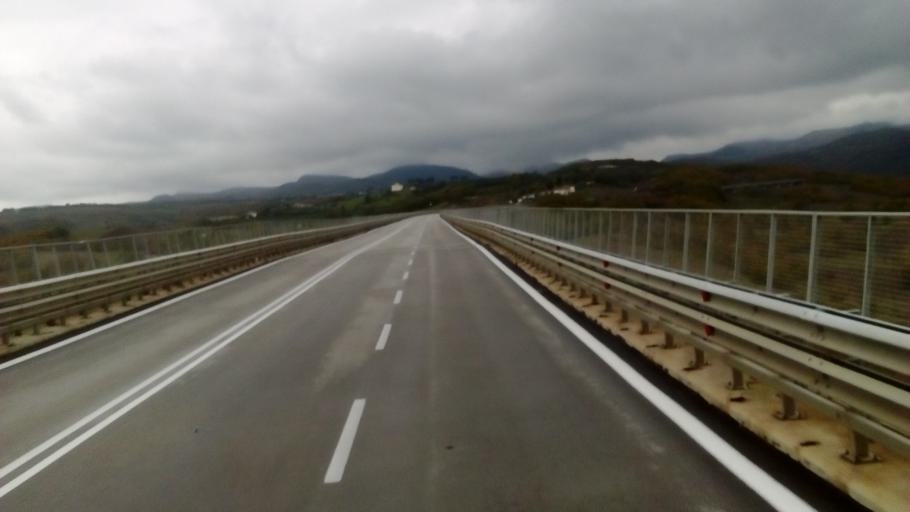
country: IT
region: Molise
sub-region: Provincia di Isernia
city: Bagnoli del Trigno
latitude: 41.7274
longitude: 14.4555
